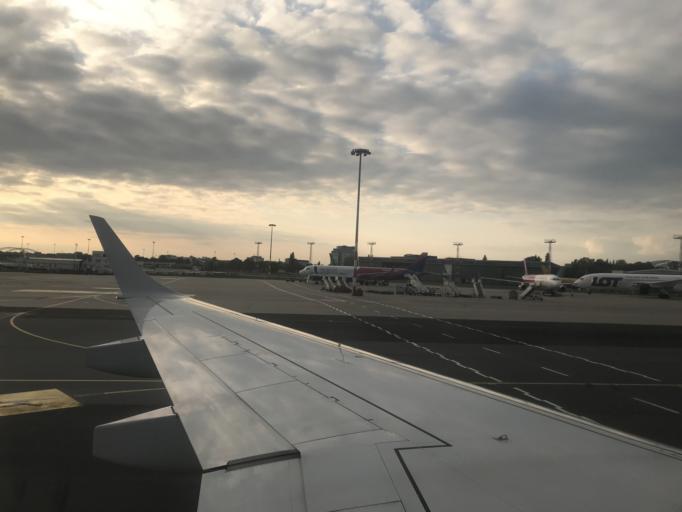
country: PL
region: Masovian Voivodeship
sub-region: Warszawa
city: Wlochy
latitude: 52.1758
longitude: 20.9684
